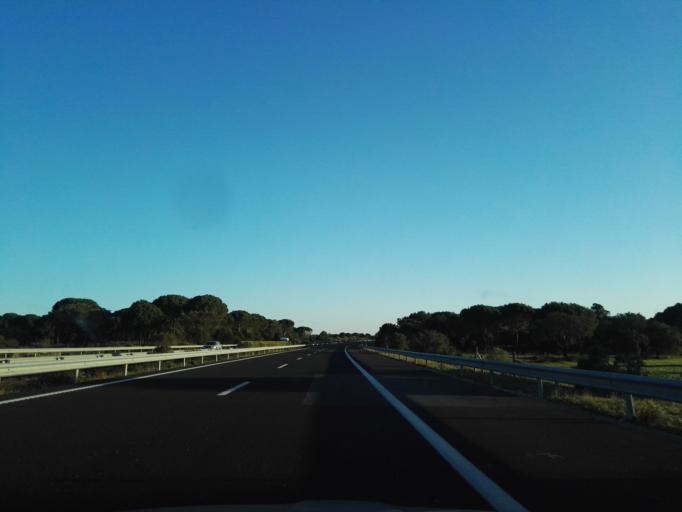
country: PT
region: Evora
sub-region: Vendas Novas
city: Vendas Novas
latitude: 38.7045
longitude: -8.6428
